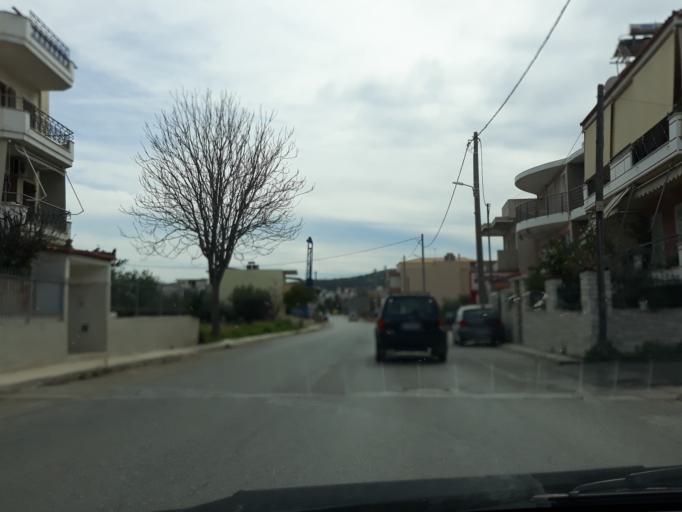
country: GR
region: Attica
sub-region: Nomarchia Dytikis Attikis
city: Ano Liosia
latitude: 38.0824
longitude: 23.7106
